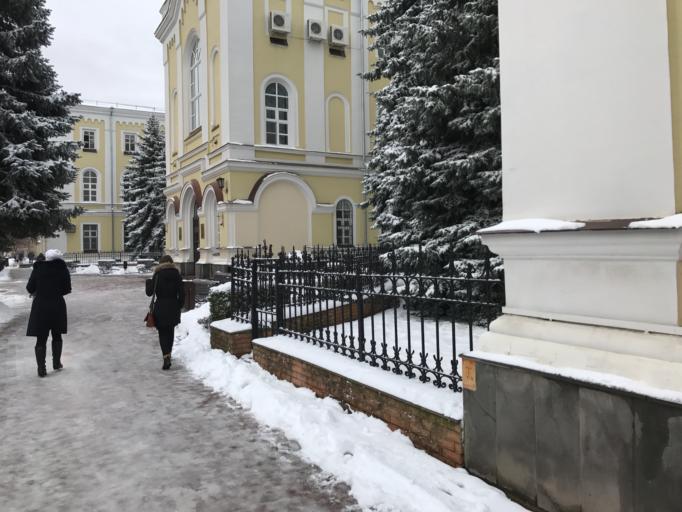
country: RU
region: Stavropol'skiy
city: Stavropol'
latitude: 45.0430
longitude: 41.9625
